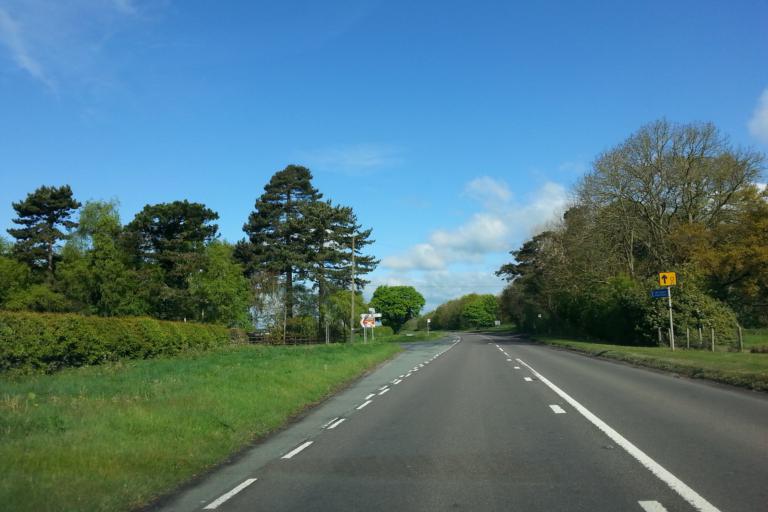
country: GB
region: England
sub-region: Staffordshire
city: Alrewas
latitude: 52.7392
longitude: -1.7826
